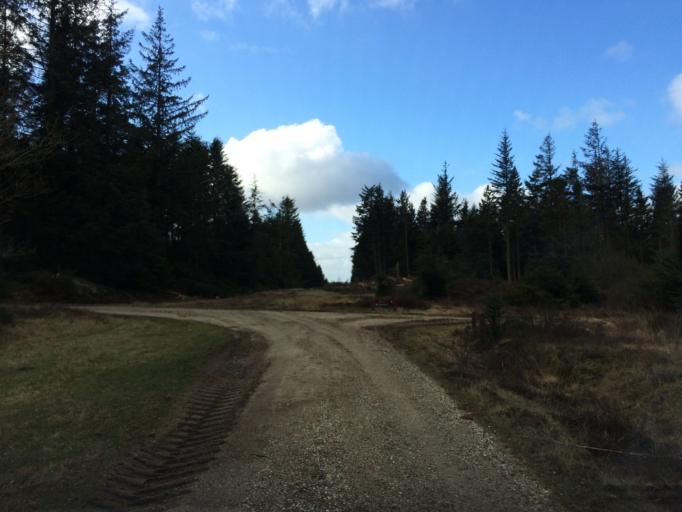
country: DK
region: Central Jutland
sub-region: Holstebro Kommune
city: Ulfborg
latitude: 56.2518
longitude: 8.4453
